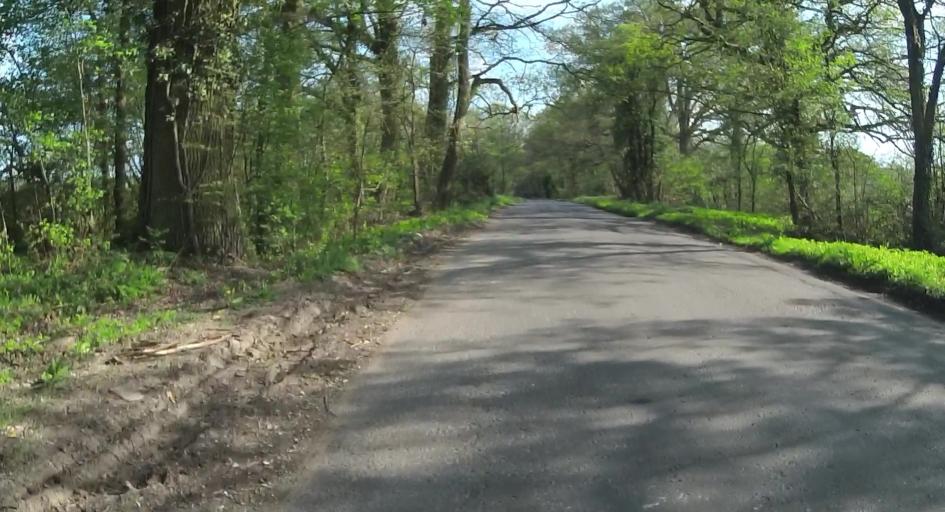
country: GB
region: England
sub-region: West Berkshire
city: Stratfield Mortimer
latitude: 51.3421
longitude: -1.0676
